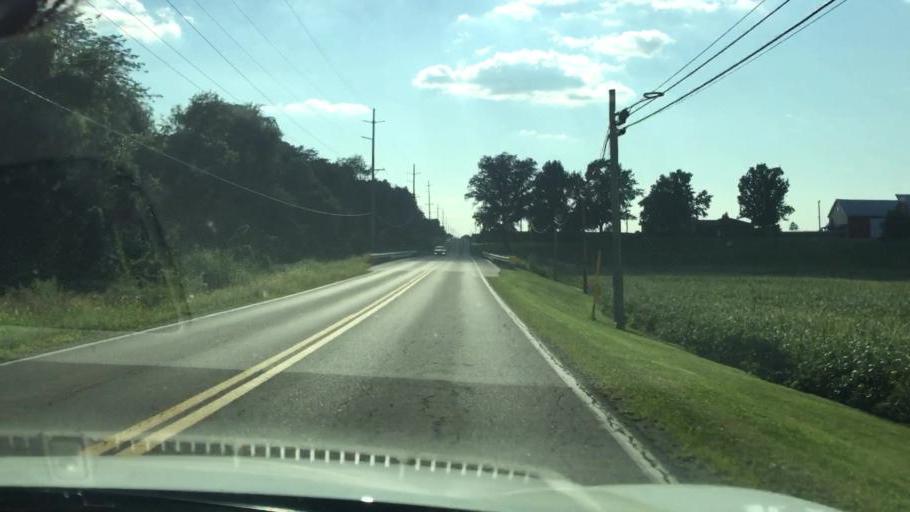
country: US
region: Ohio
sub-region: Clark County
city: Northridge
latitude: 39.9390
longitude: -83.7133
